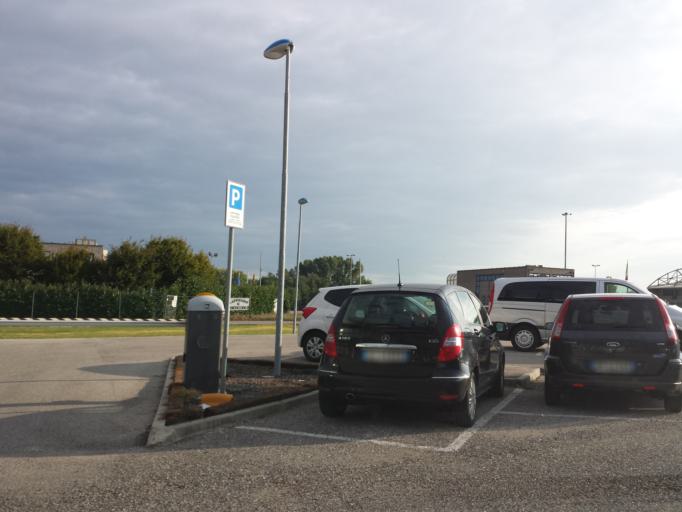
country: IT
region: Veneto
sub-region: Provincia di Rovigo
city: Pontecchio Polesine
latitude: 45.0351
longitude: 11.8095
